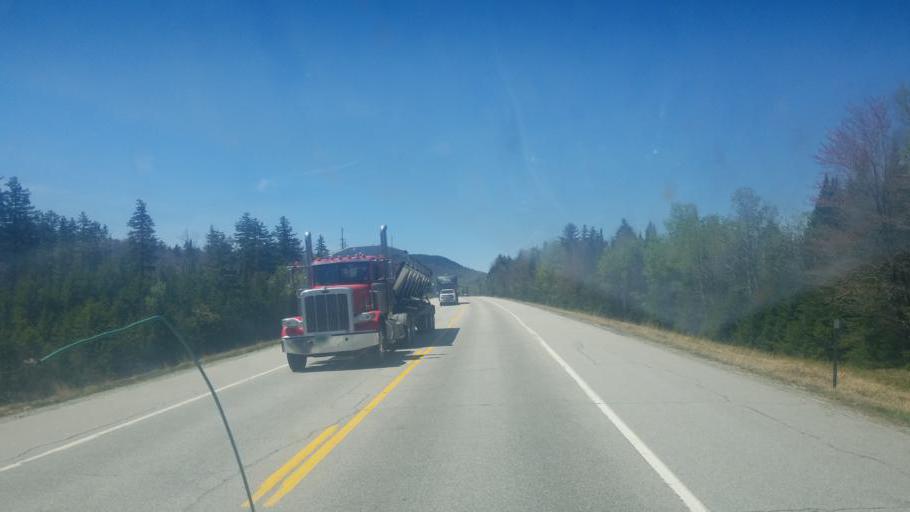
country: US
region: New Hampshire
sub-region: Grafton County
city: Deerfield
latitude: 44.2687
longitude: -71.4791
